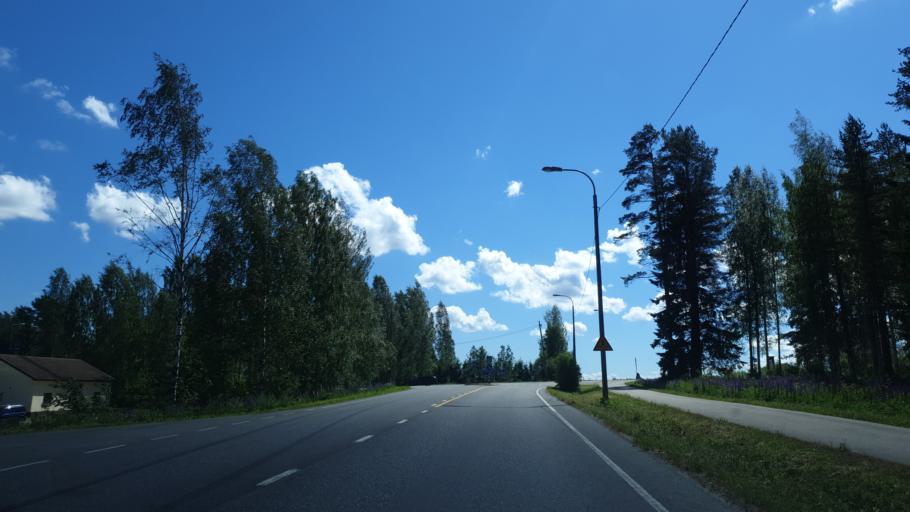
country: FI
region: Northern Savo
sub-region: Koillis-Savo
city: Kaavi
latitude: 62.9757
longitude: 28.4932
